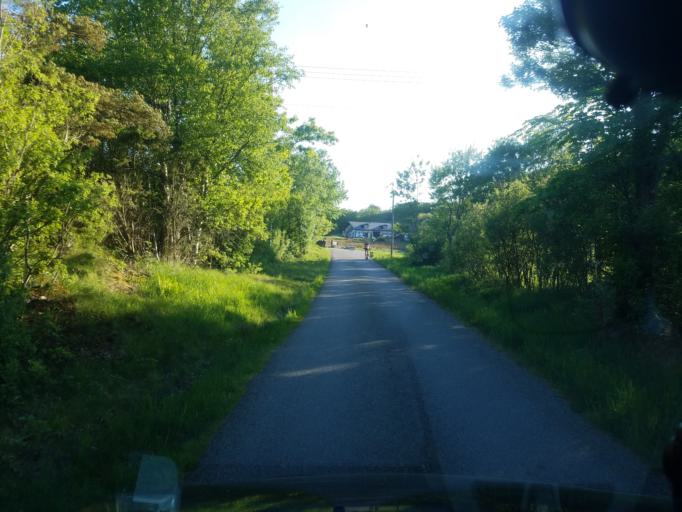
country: SE
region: Vaestra Goetaland
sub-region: Lysekils Kommun
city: Lysekil
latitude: 58.3043
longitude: 11.4573
